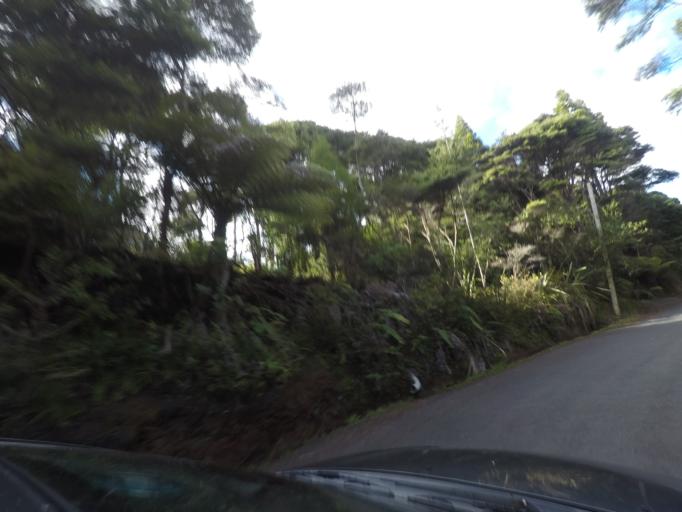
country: NZ
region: Auckland
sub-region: Auckland
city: Titirangi
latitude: -37.0170
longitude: 174.5520
